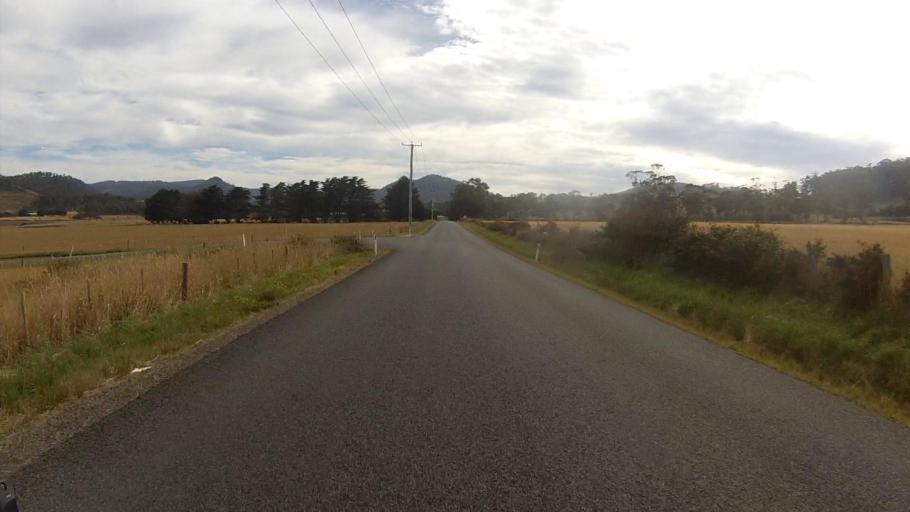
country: AU
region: Tasmania
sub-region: Sorell
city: Sorell
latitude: -42.7951
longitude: 147.7951
